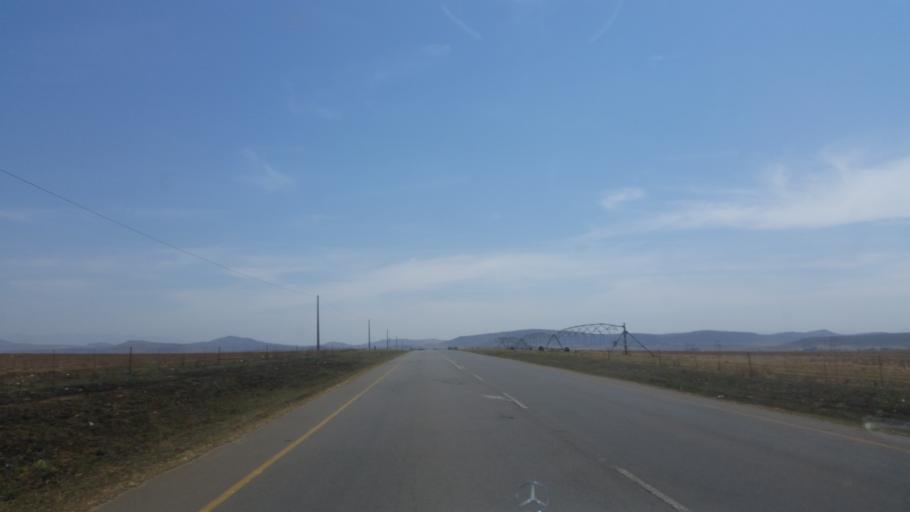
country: ZA
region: KwaZulu-Natal
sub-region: uThukela District Municipality
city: Bergville
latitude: -28.8205
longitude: 29.5639
